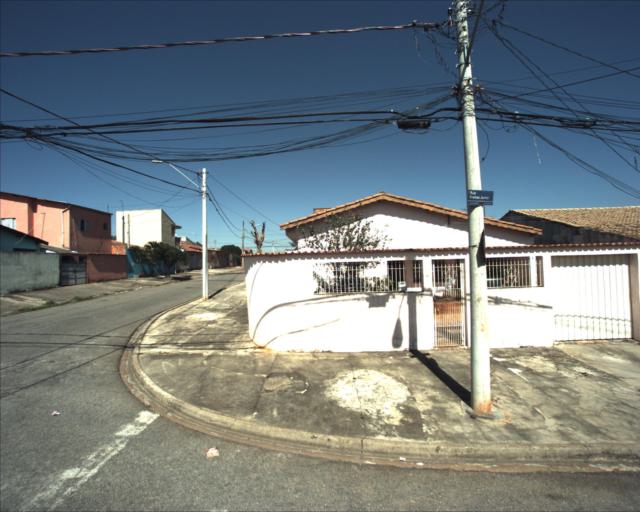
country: BR
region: Sao Paulo
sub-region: Sorocaba
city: Sorocaba
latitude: -23.4655
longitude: -47.4867
